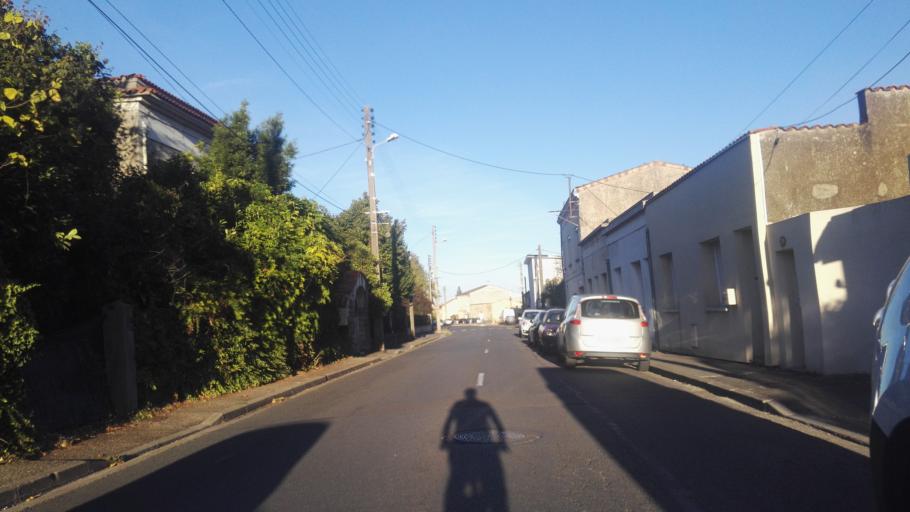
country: FR
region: Aquitaine
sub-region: Departement de la Gironde
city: Talence
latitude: 44.8066
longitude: -0.5785
